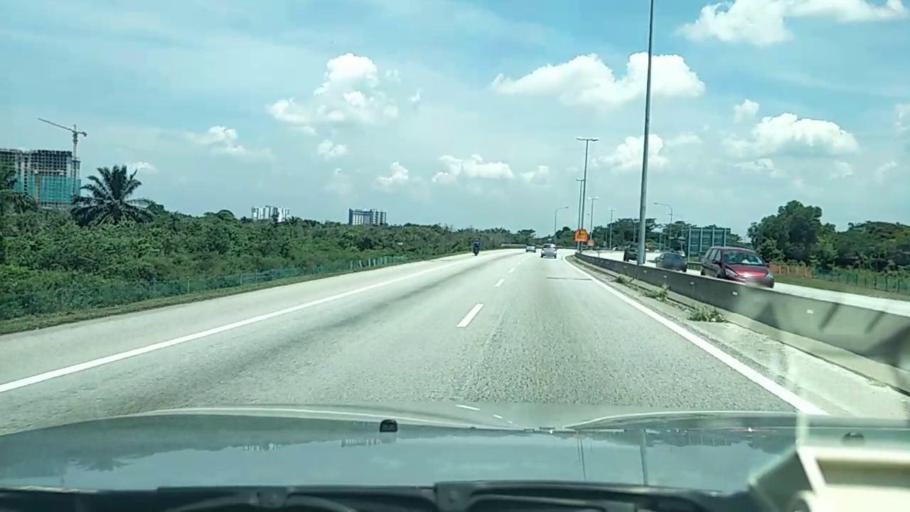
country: MY
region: Putrajaya
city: Putrajaya
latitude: 2.9341
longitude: 101.6261
